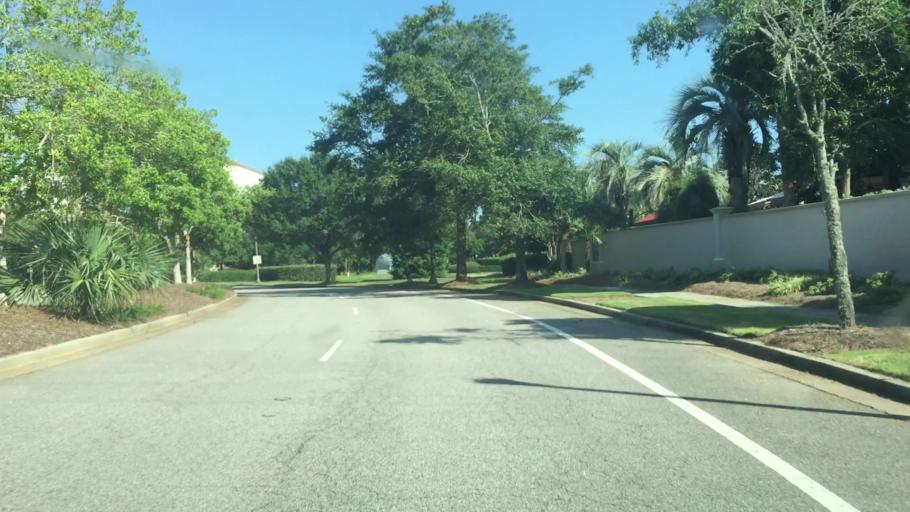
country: US
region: South Carolina
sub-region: Horry County
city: Myrtle Beach
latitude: 33.7499
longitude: -78.8119
